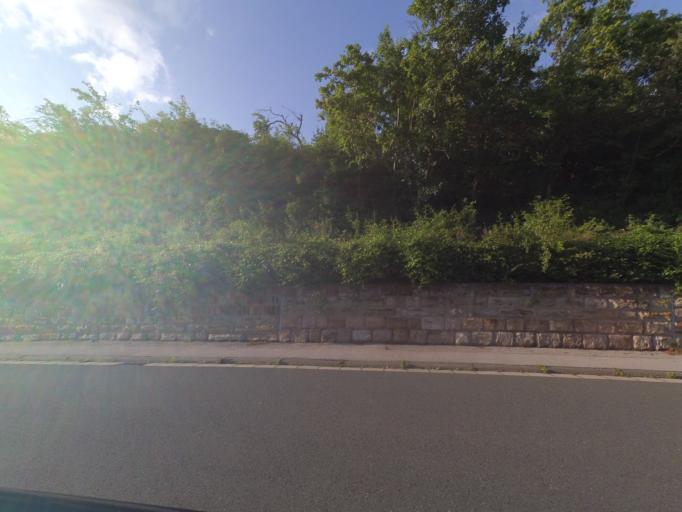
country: DE
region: Bavaria
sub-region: Regierungsbezirk Unterfranken
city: Zeil
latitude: 50.0001
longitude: 10.6185
